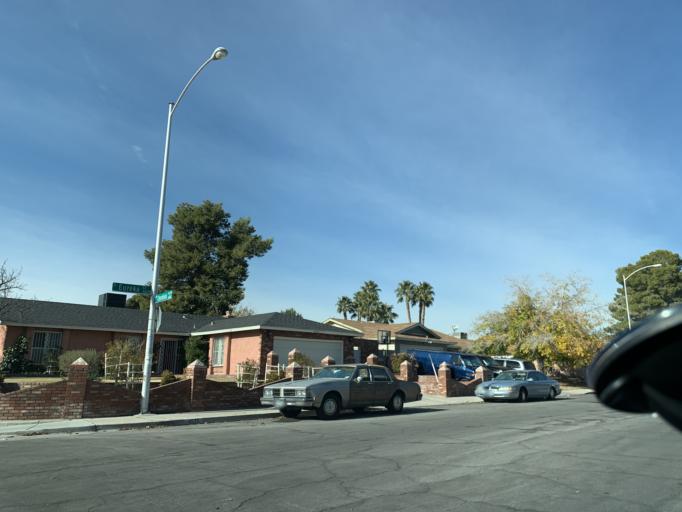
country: US
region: Nevada
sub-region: Clark County
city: Spring Valley
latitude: 36.1056
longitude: -115.2265
